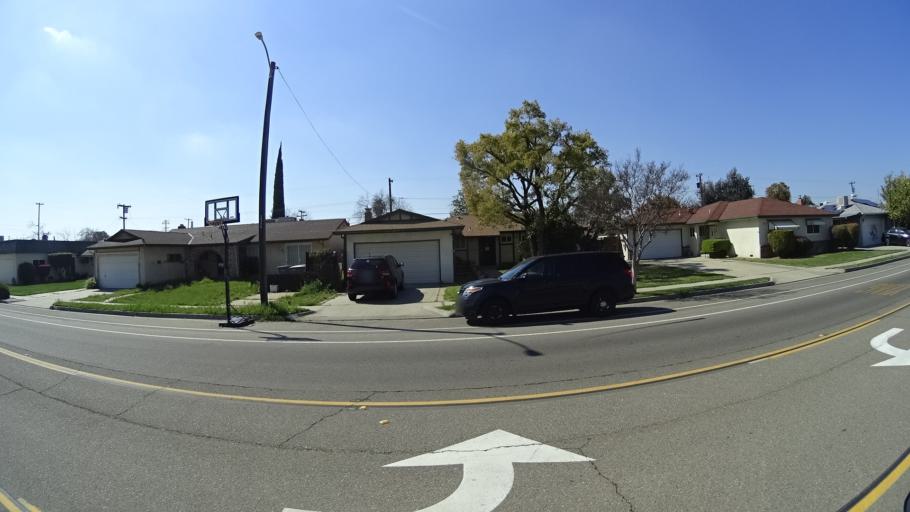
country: US
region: California
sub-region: Fresno County
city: Tarpey Village
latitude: 36.7982
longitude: -119.7363
